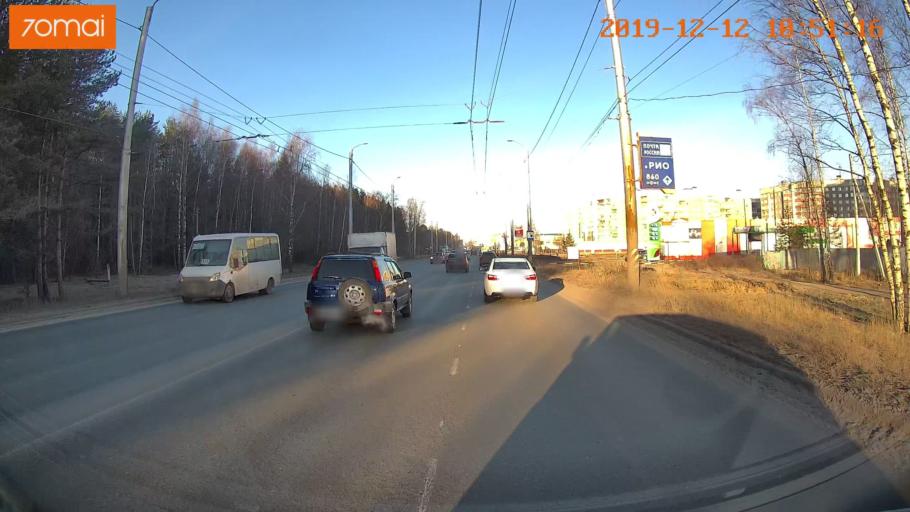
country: RU
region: Ivanovo
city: Kokhma
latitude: 56.9525
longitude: 41.0449
